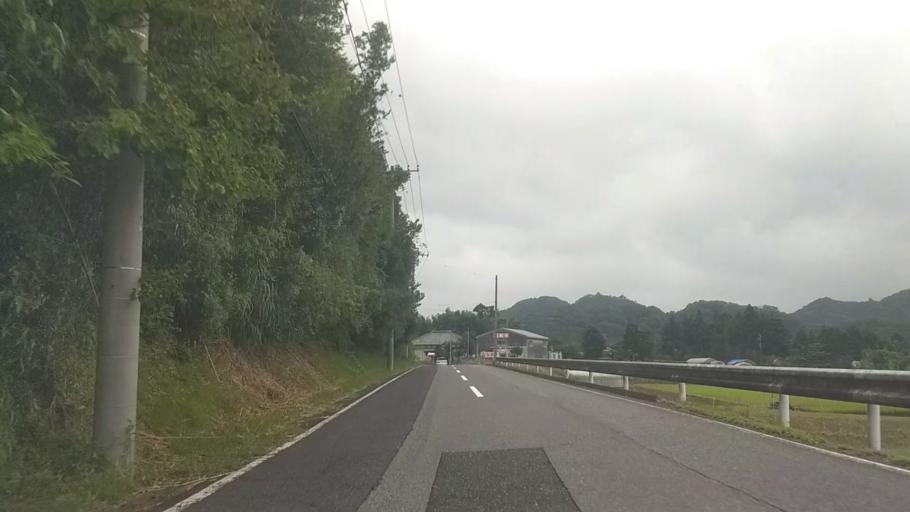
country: JP
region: Chiba
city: Kawaguchi
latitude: 35.2248
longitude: 140.0166
